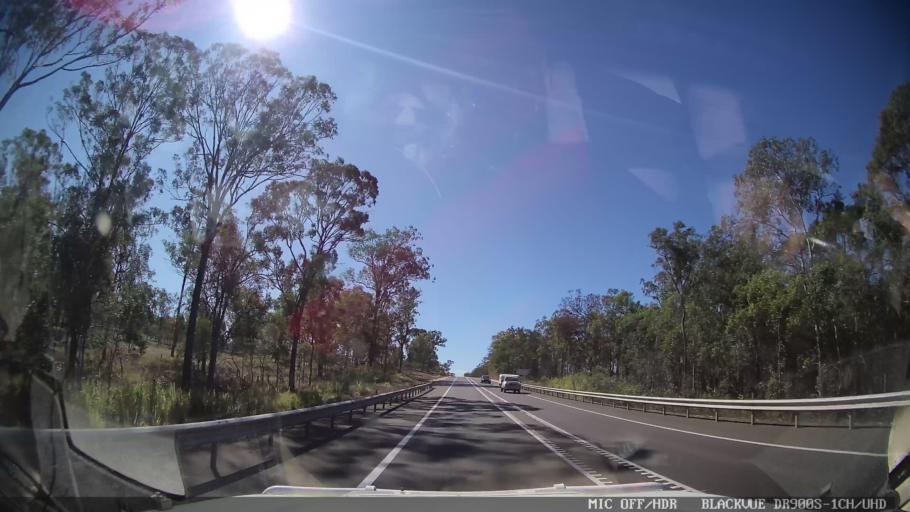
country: AU
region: Queensland
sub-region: Fraser Coast
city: Maryborough
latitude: -25.6536
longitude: 152.6302
